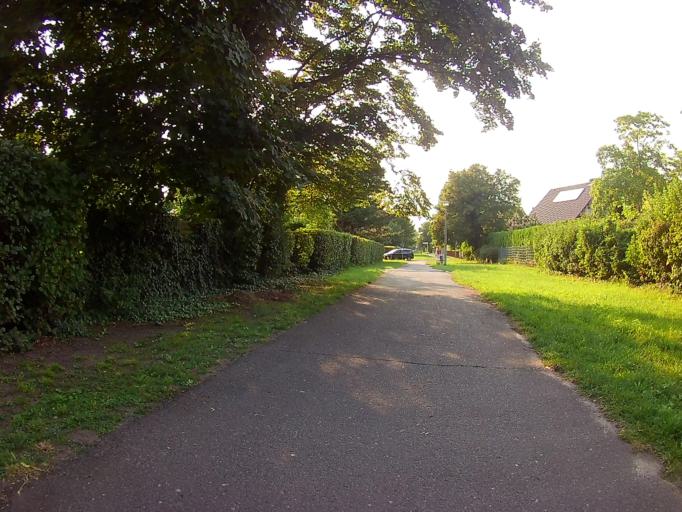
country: DE
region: Berlin
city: Biesdorf
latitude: 52.5205
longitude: 13.5498
